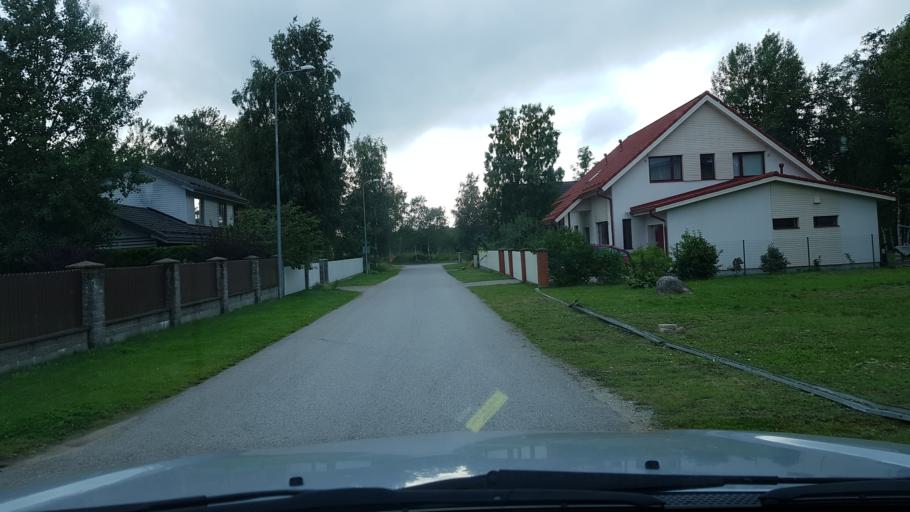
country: EE
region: Harju
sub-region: Rae vald
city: Jueri
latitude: 59.3956
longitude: 24.8398
